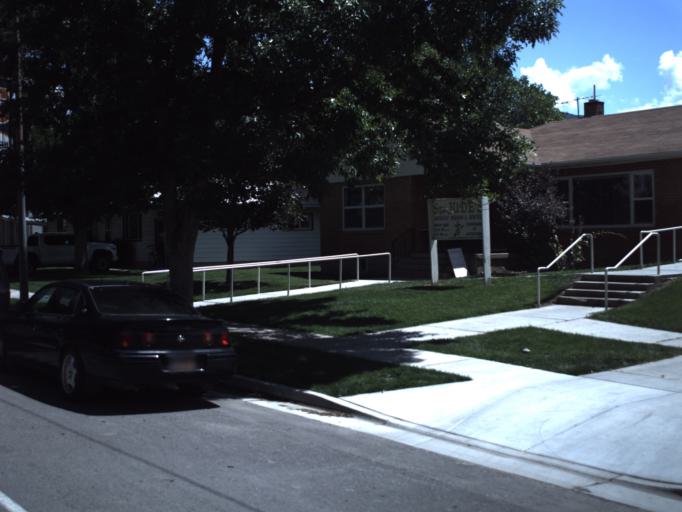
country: US
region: Utah
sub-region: Sanpete County
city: Ephraim
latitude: 39.3597
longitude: -111.5830
